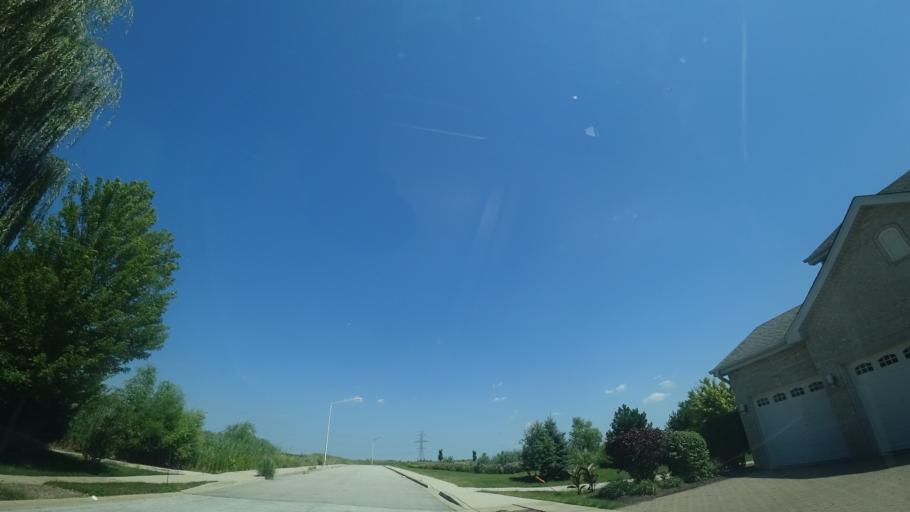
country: US
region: Illinois
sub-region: Will County
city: Mokena
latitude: 41.5591
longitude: -87.8857
